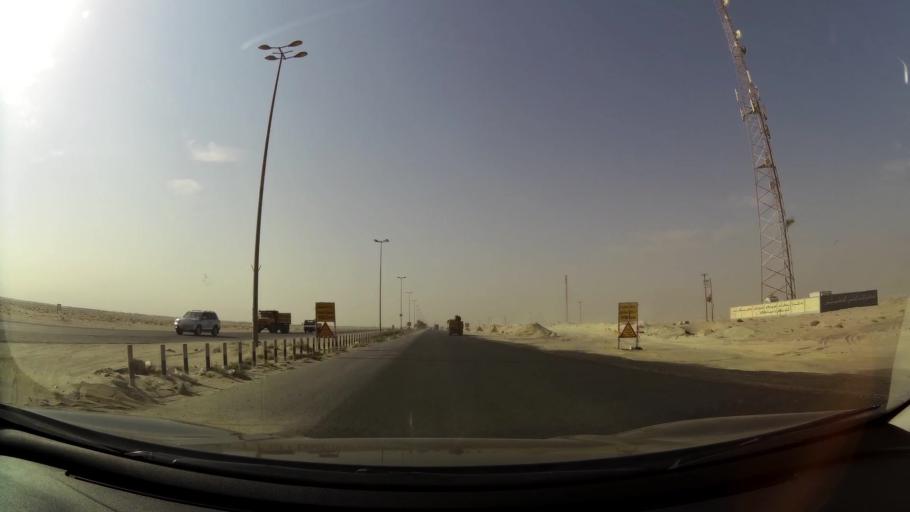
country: KW
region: Al Ahmadi
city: Al Ahmadi
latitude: 28.9054
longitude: 48.0935
